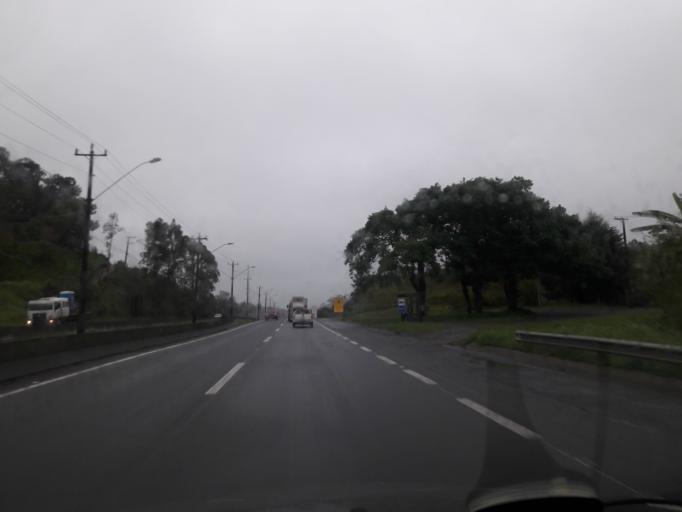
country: BR
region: Sao Paulo
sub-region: Itapecerica Da Serra
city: Itapecerica da Serra
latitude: -23.7536
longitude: -46.9016
